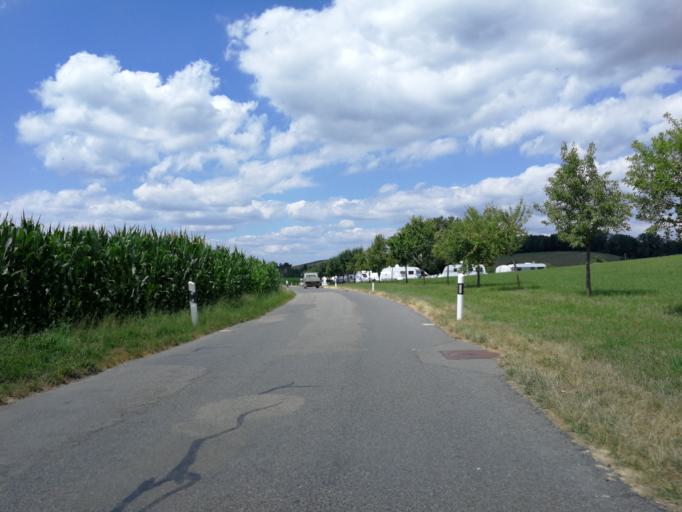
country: CH
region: Zurich
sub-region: Bezirk Hinwil
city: Gruet
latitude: 47.2872
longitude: 8.7855
